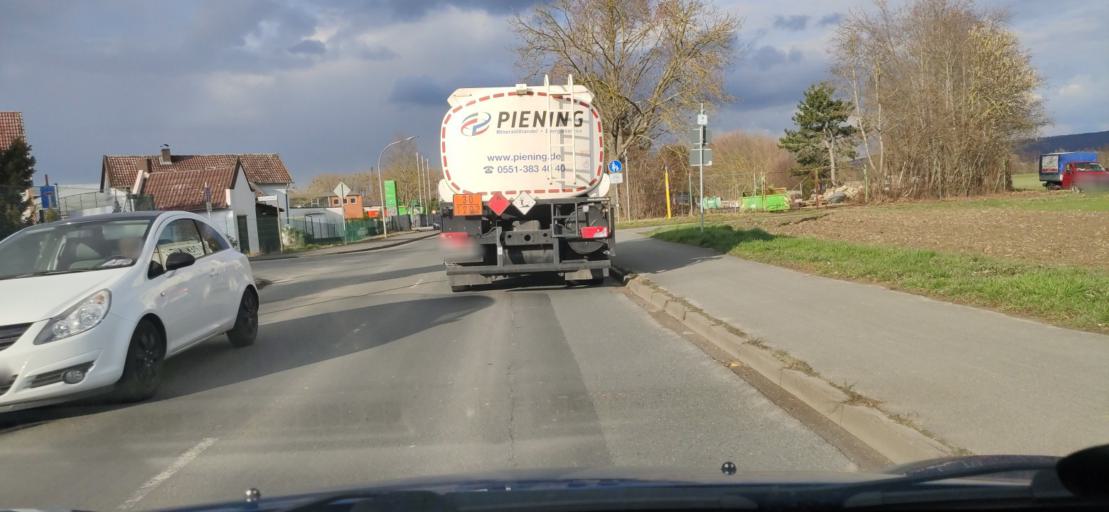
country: DE
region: Lower Saxony
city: Rosdorf
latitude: 51.5079
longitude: 9.9139
